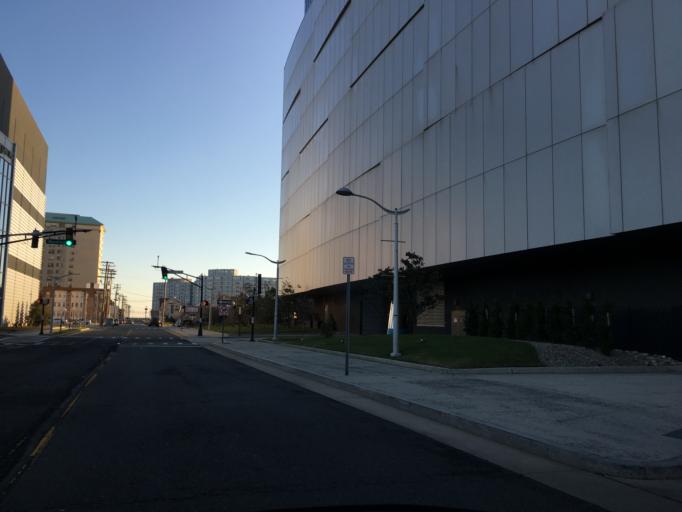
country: US
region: New Jersey
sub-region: Atlantic County
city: Atlantic City
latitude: 39.3638
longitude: -74.4155
